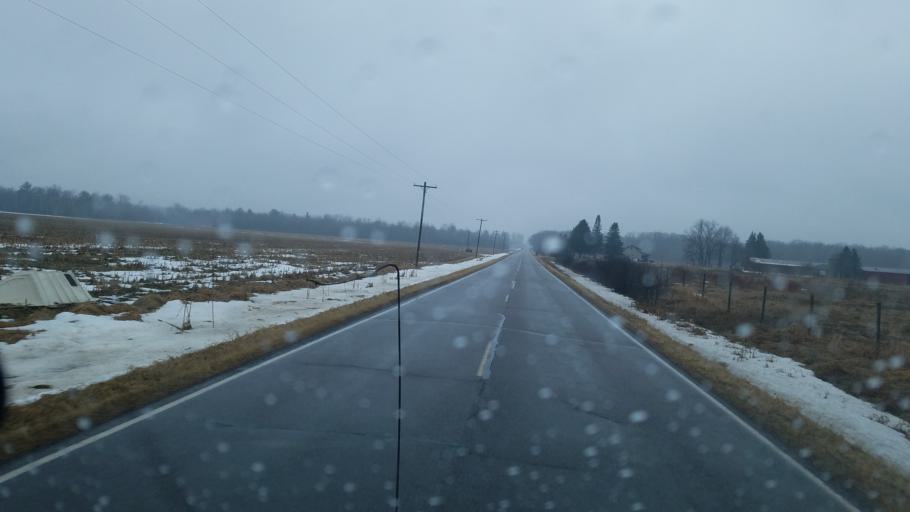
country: US
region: Wisconsin
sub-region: Wood County
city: Marshfield
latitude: 44.4843
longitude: -90.2798
